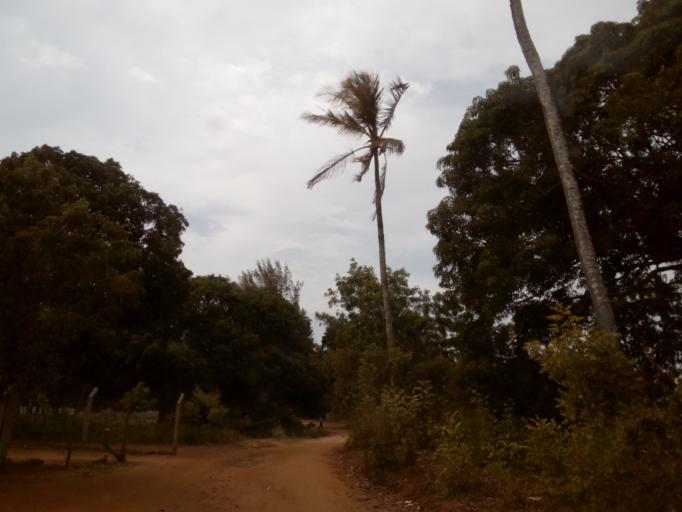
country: TZ
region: Zanzibar Central/South
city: Mahonda
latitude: -6.3374
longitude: 39.4057
